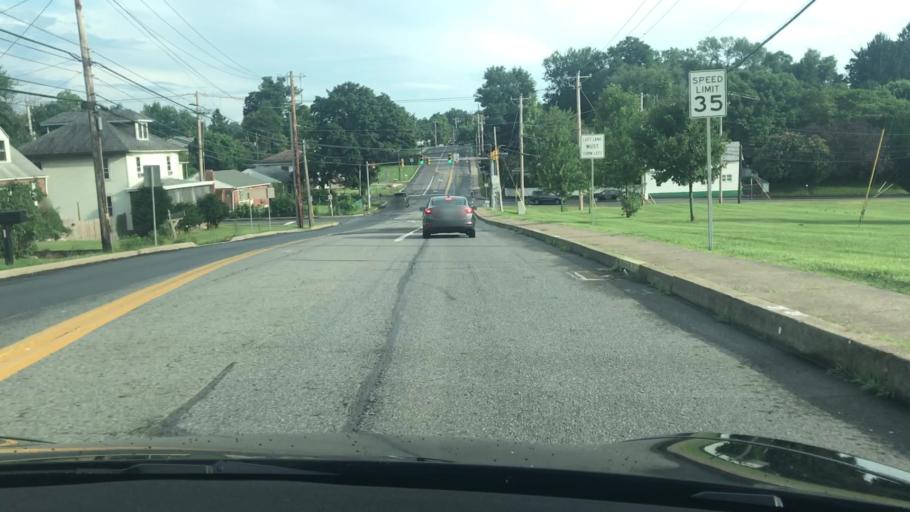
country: US
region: Pennsylvania
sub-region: Dauphin County
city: Colonial Park
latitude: 40.3056
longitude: -76.8230
